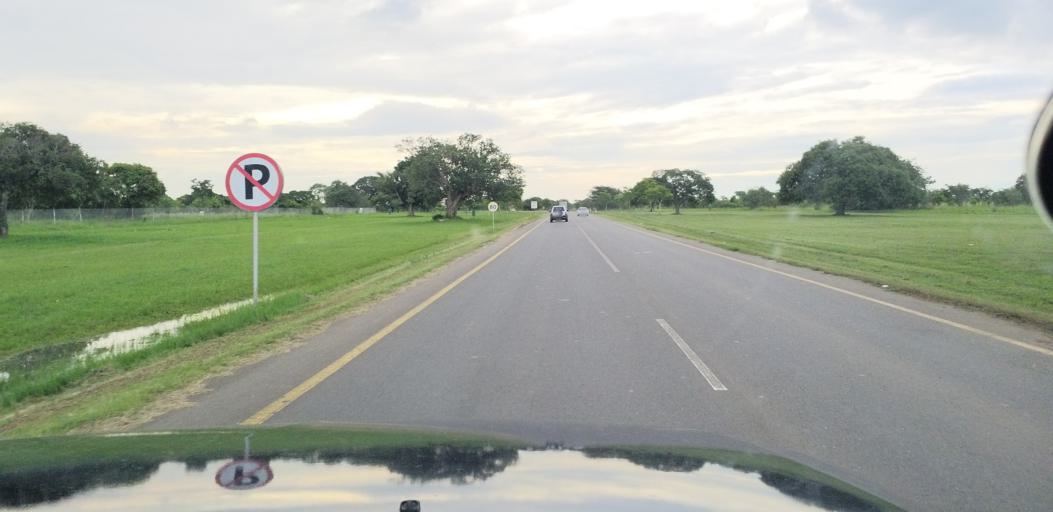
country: ZM
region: Lusaka
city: Lusaka
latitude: -15.3187
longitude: 28.4259
